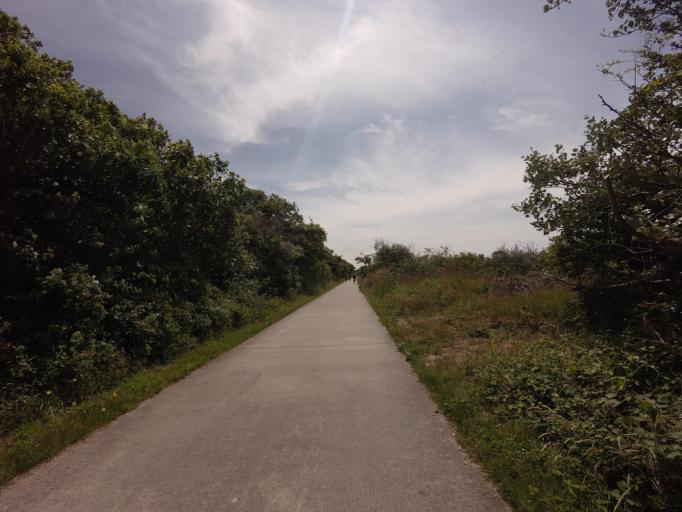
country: NL
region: North Holland
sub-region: Gemeente Texel
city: Den Burg
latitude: 53.1622
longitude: 4.8432
